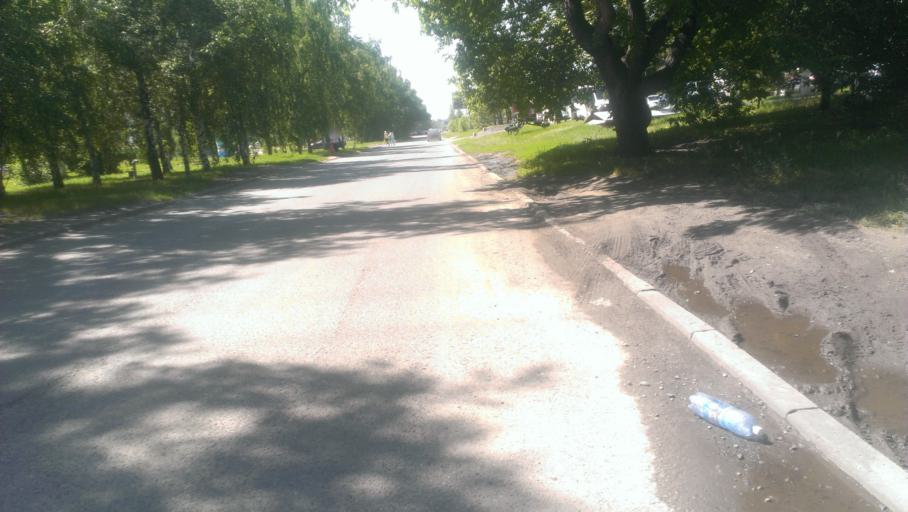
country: RU
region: Altai Krai
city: Novosilikatnyy
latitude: 53.3435
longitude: 83.6792
